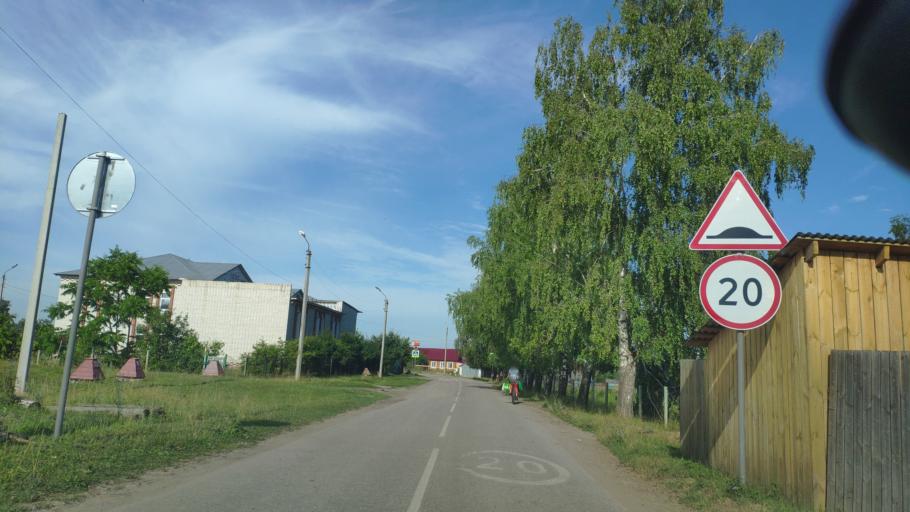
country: RU
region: Nizjnij Novgorod
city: Vorotynets
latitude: 56.1886
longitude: 45.7823
